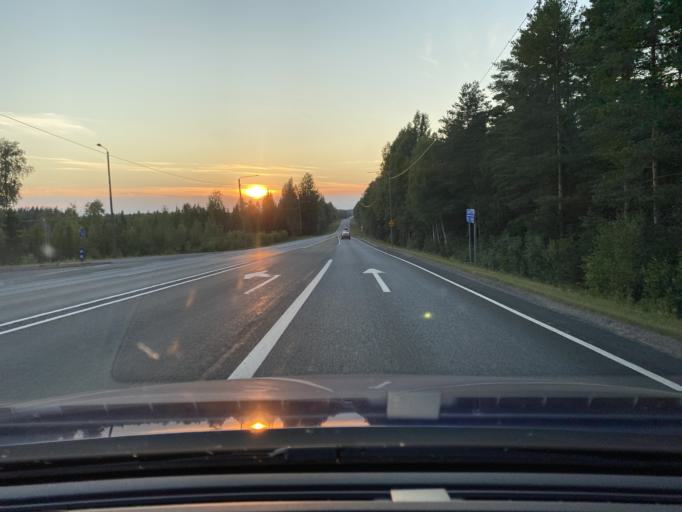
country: FI
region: Pirkanmaa
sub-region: Luoteis-Pirkanmaa
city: Ikaalinen
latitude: 61.7881
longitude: 22.9921
